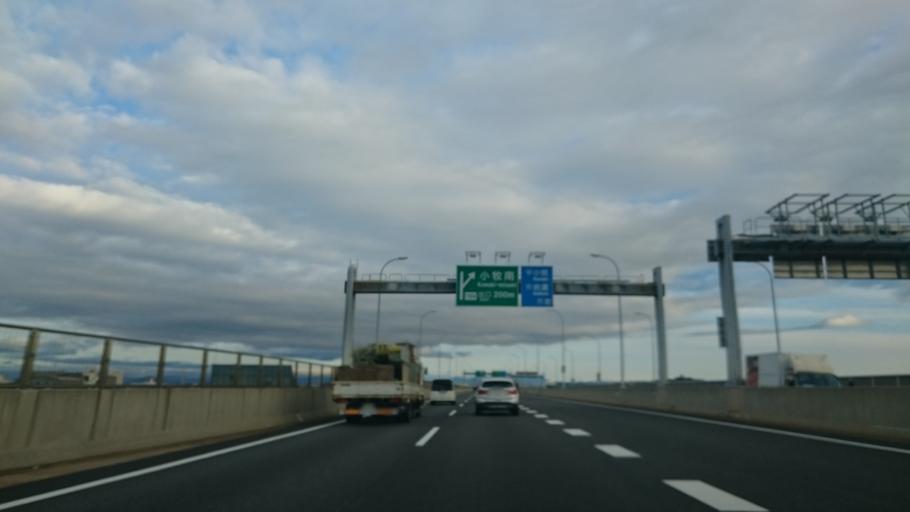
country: JP
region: Aichi
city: Komaki
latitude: 35.2670
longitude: 136.9077
